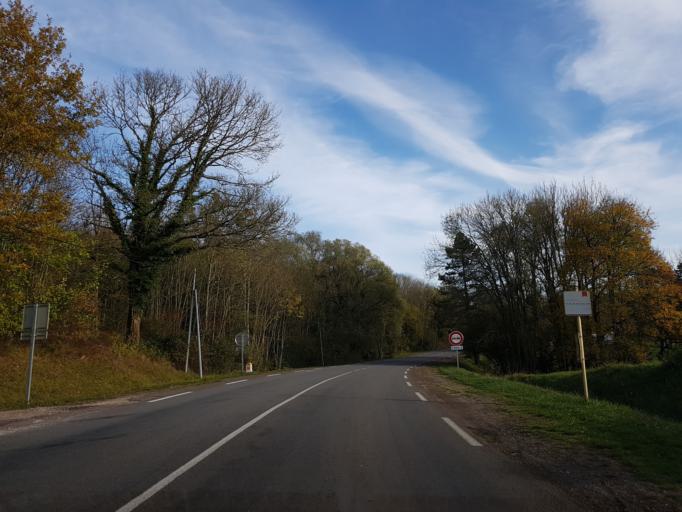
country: FR
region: Bourgogne
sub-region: Departement de la Cote-d'Or
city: Pouilly-en-Auxois
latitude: 47.3148
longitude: 4.6061
